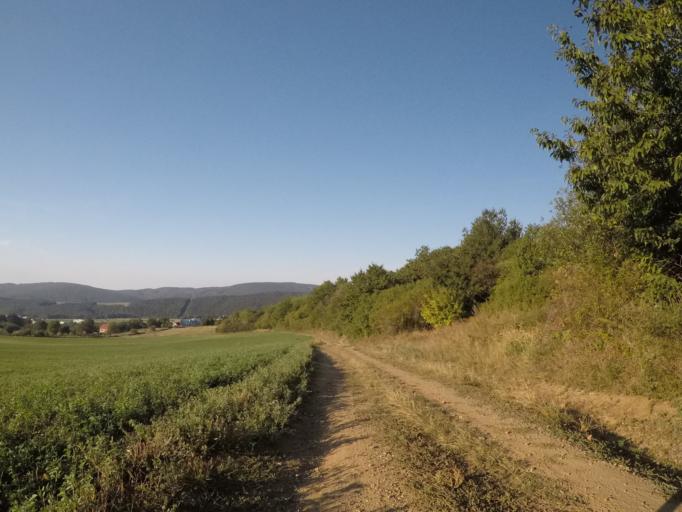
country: SK
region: Kosicky
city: Kosice
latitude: 48.7493
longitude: 21.1274
